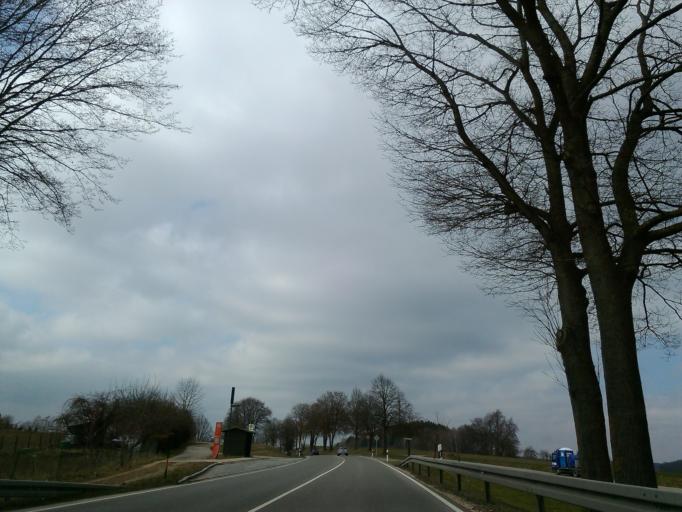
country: DE
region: Bavaria
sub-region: Swabia
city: Krumbach
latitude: 48.2450
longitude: 10.3856
